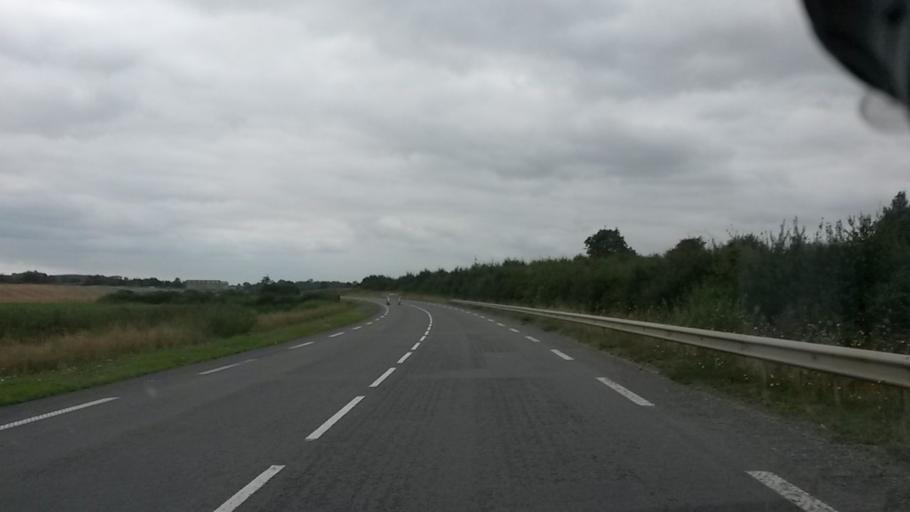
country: FR
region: Nord-Pas-de-Calais
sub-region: Departement du Pas-de-Calais
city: Bapaume
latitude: 50.1150
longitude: 2.8370
